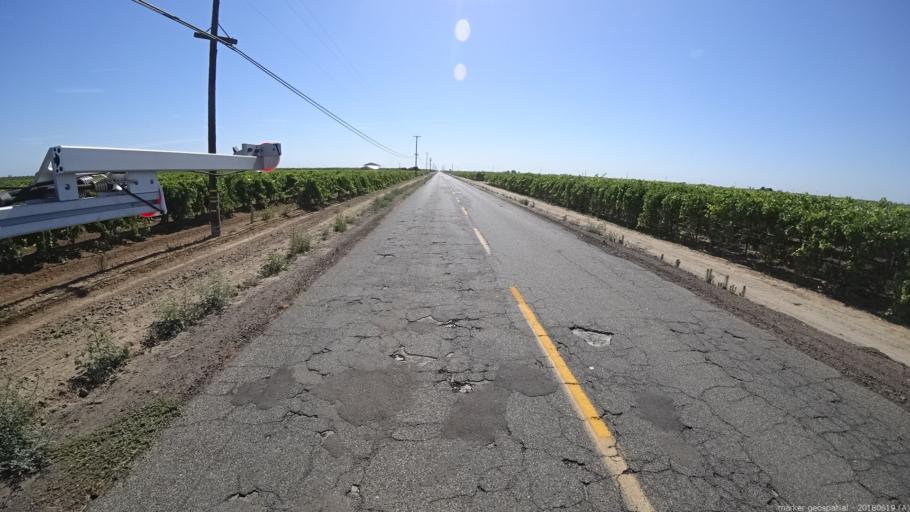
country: US
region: California
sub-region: Fresno County
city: Biola
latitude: 36.8368
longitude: -120.1227
